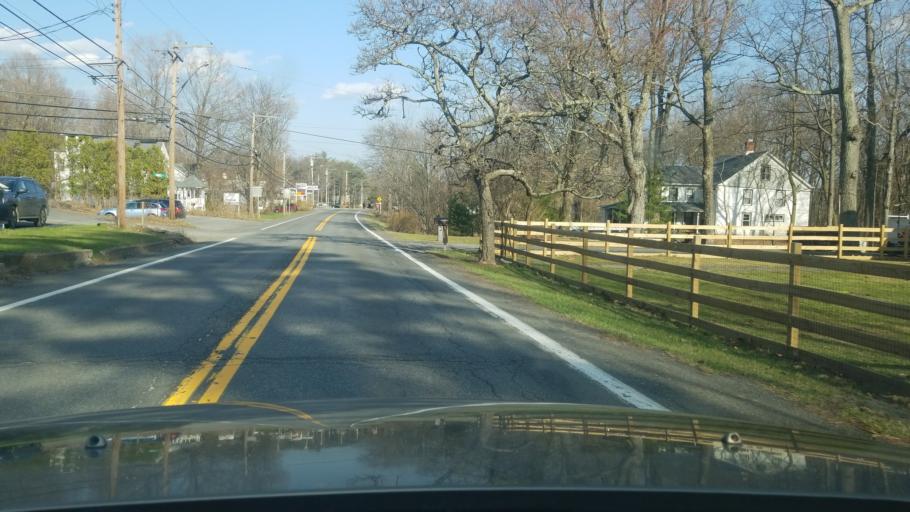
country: US
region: New York
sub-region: Greene County
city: Palenville
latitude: 42.1753
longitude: -74.0269
